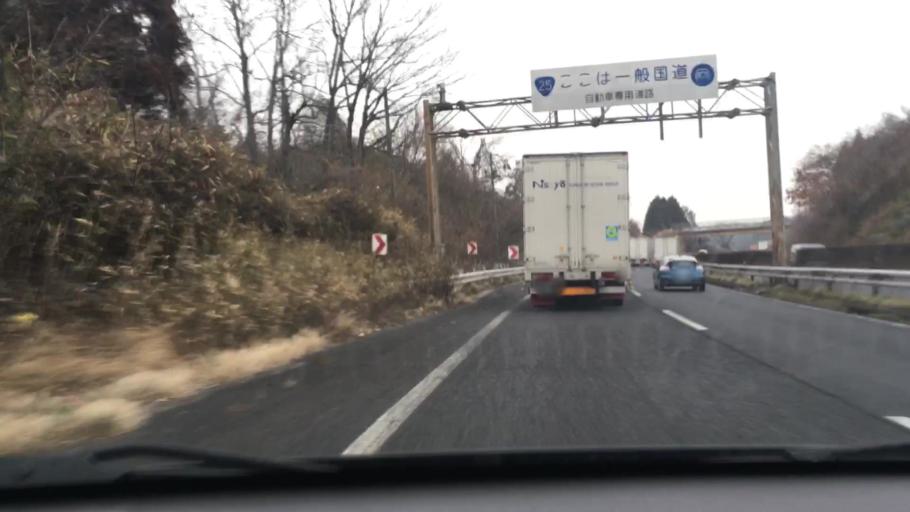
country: JP
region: Mie
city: Nabari
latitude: 34.7013
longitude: 136.0651
